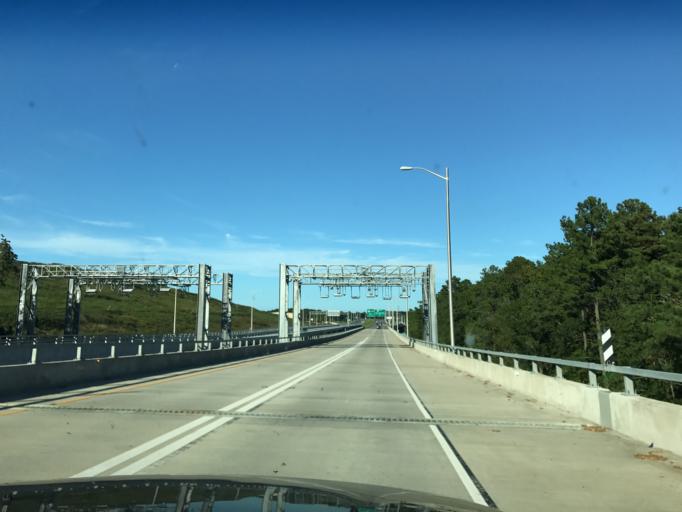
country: US
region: Virginia
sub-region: City of Chesapeake
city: Chesapeake
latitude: 36.7414
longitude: -76.2899
